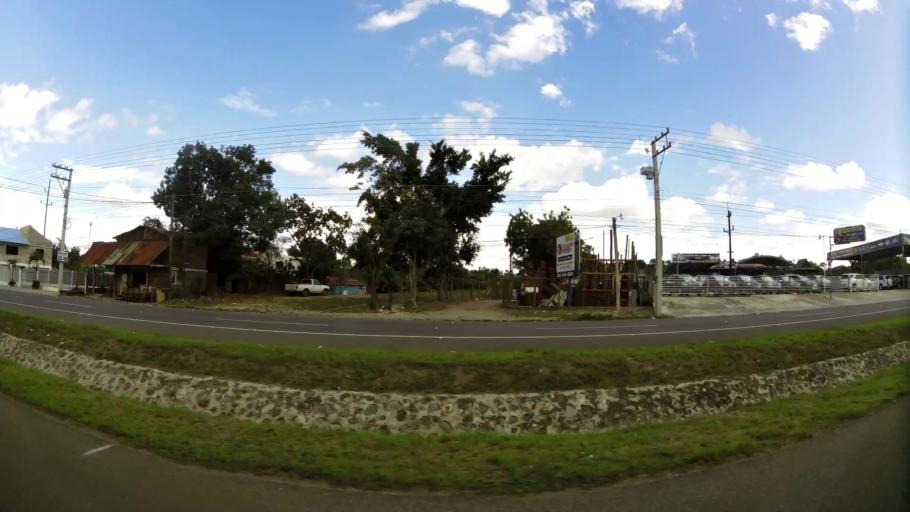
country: DO
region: La Vega
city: Rio Verde Arriba
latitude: 19.3520
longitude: -70.6006
